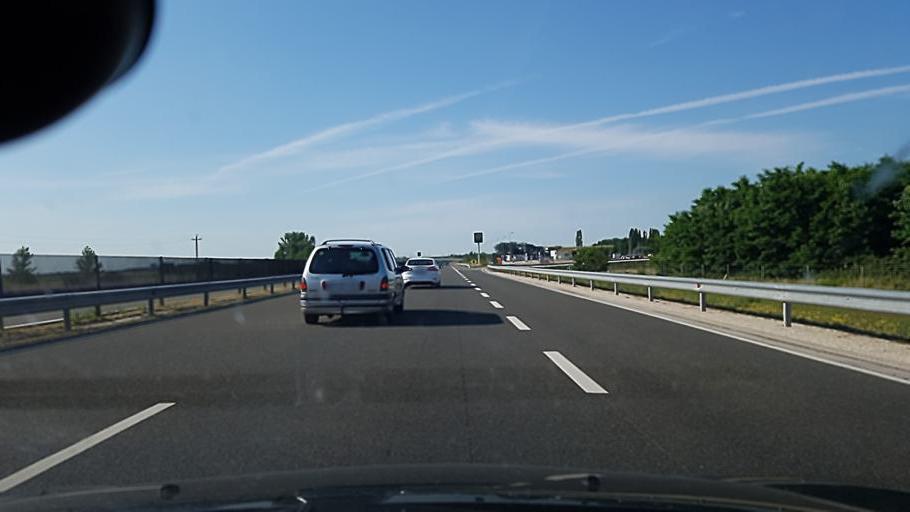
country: HU
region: Tolna
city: Paks
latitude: 46.6497
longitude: 18.8151
